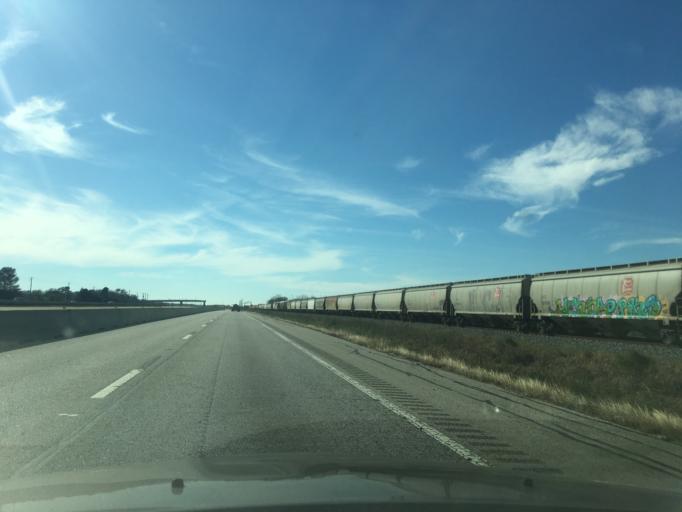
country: US
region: Texas
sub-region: Wharton County
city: East Bernard
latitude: 29.4724
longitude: -95.9591
